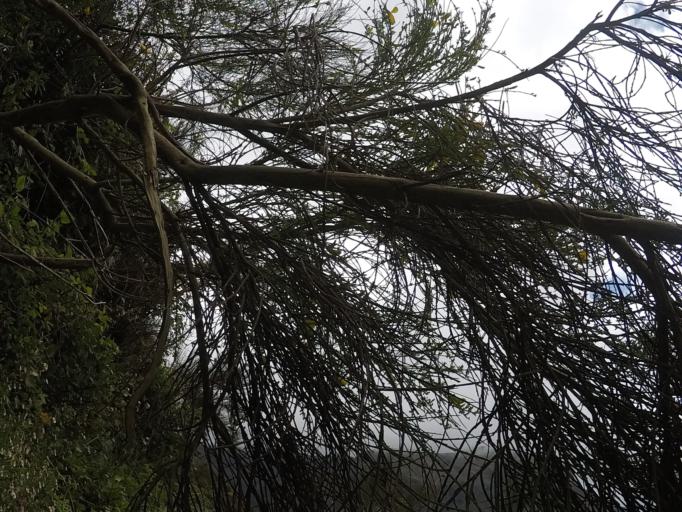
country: PT
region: Madeira
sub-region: Camara de Lobos
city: Curral das Freiras
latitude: 32.7364
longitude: -17.0001
